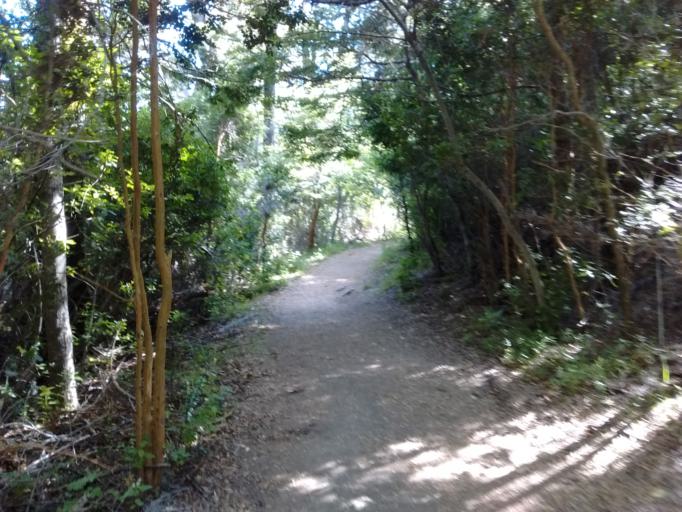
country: AR
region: Rio Negro
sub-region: Departamento de Bariloche
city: San Carlos de Bariloche
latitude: -41.0630
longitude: -71.5682
